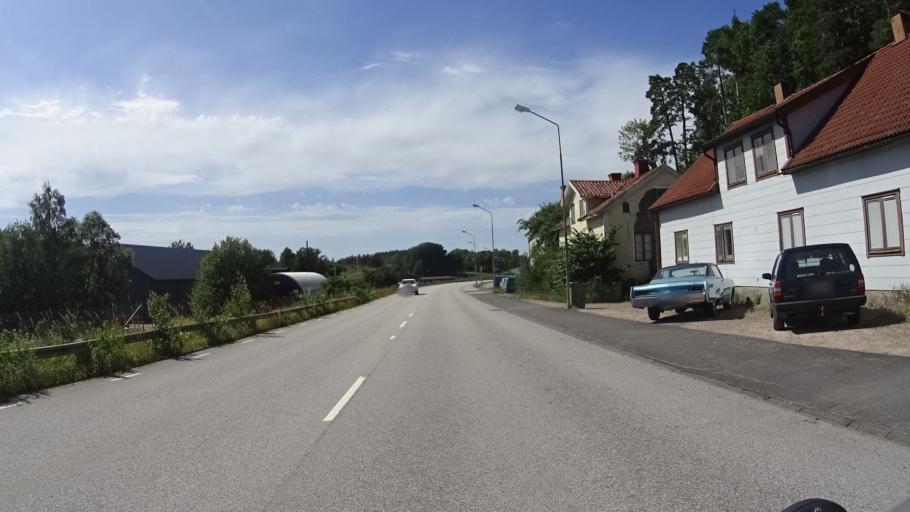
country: SE
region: Kalmar
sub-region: Vasterviks Kommun
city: Gamleby
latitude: 57.9015
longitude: 16.4025
